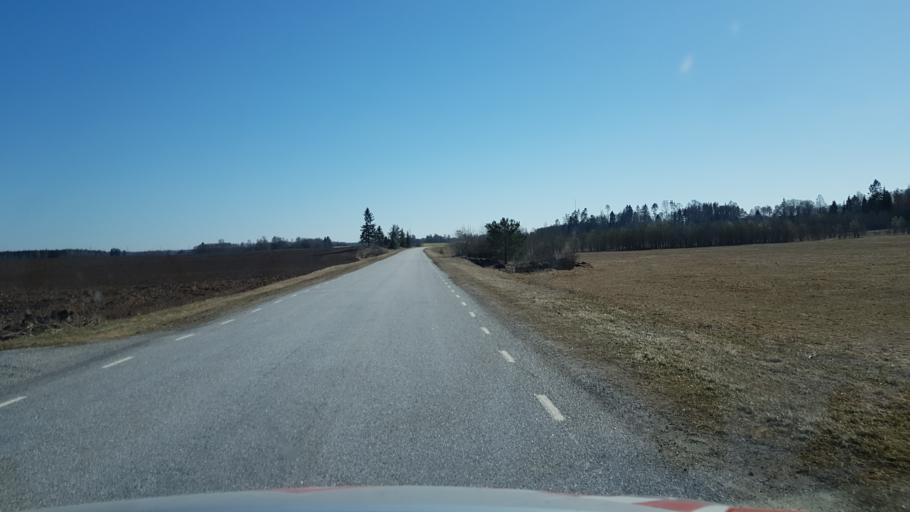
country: EE
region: Jaervamaa
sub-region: Koeru vald
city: Koeru
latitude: 59.0335
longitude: 26.0908
